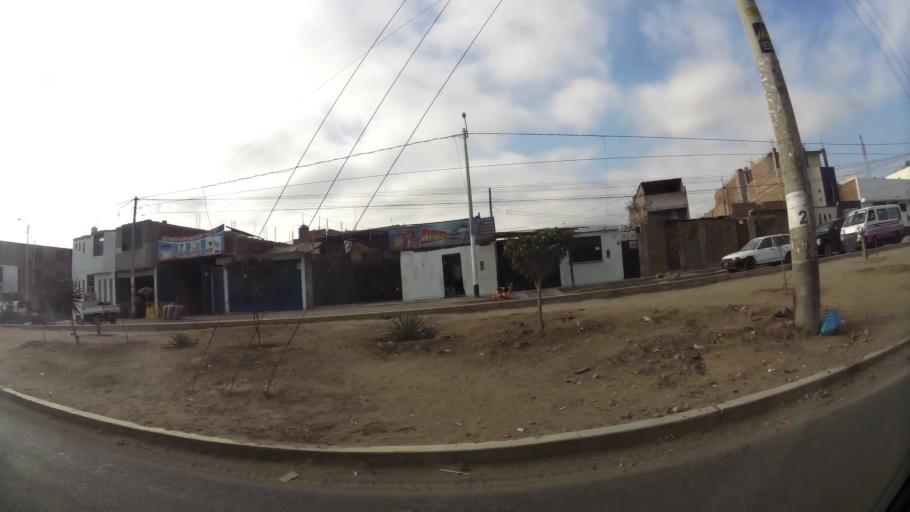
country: PE
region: La Libertad
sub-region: Provincia de Trujillo
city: La Esperanza
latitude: -8.0912
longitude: -79.0449
